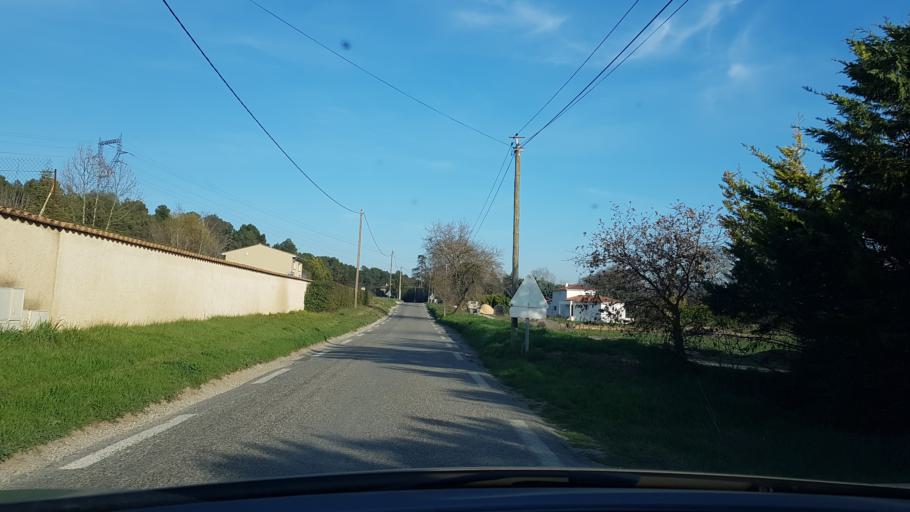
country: FR
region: Provence-Alpes-Cote d'Azur
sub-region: Departement des Bouches-du-Rhone
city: Cabries
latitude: 43.4579
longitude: 5.3761
